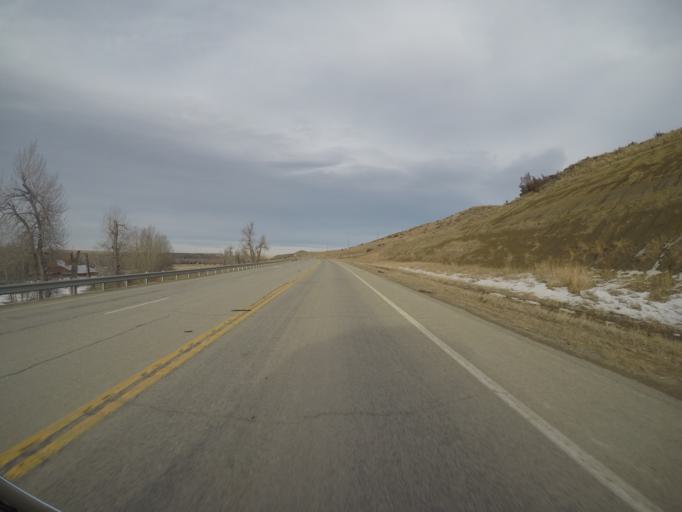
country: US
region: Montana
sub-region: Stillwater County
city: Absarokee
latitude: 45.4937
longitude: -109.4509
